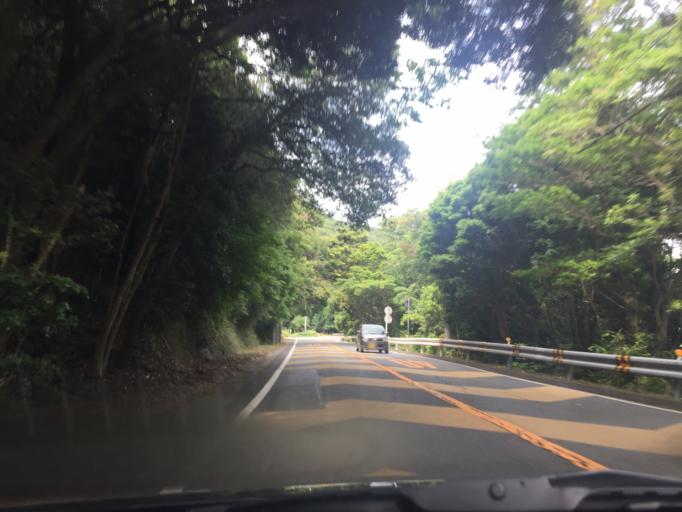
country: JP
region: Shizuoka
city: Shimoda
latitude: 34.7123
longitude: 138.9821
